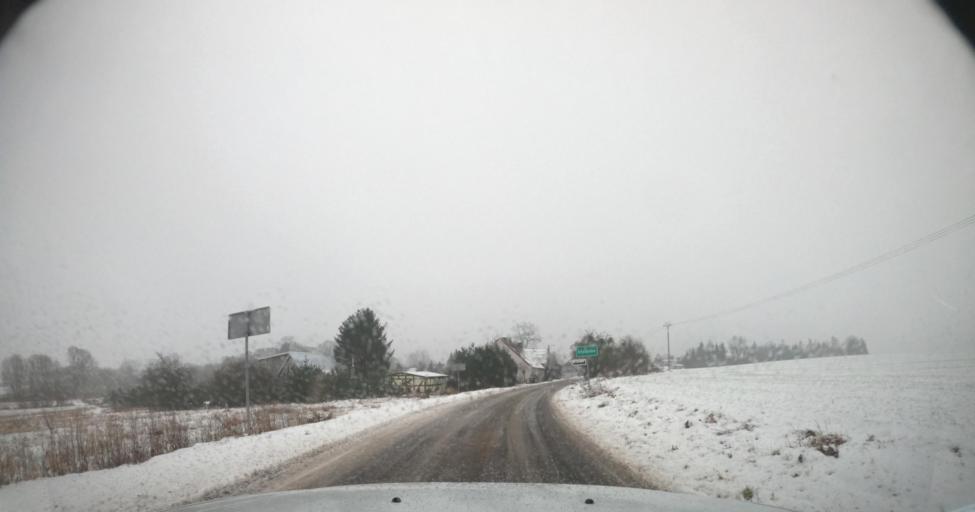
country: PL
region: West Pomeranian Voivodeship
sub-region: Powiat kamienski
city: Golczewo
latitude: 53.7907
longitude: 14.9521
